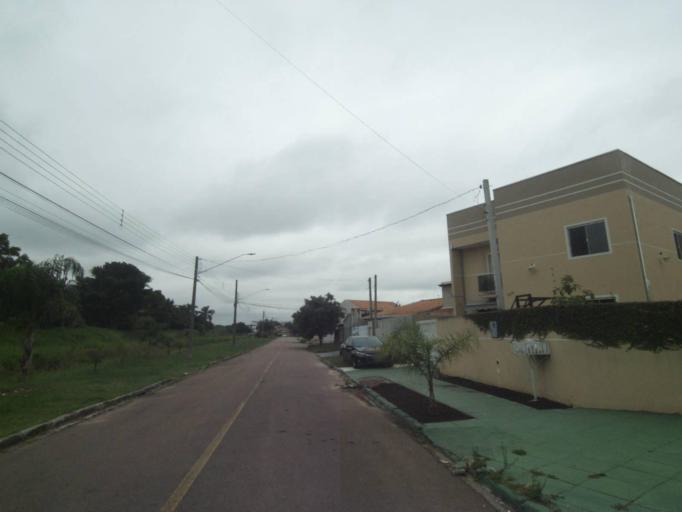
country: BR
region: Parana
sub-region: Araucaria
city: Araucaria
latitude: -25.5415
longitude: -49.3432
